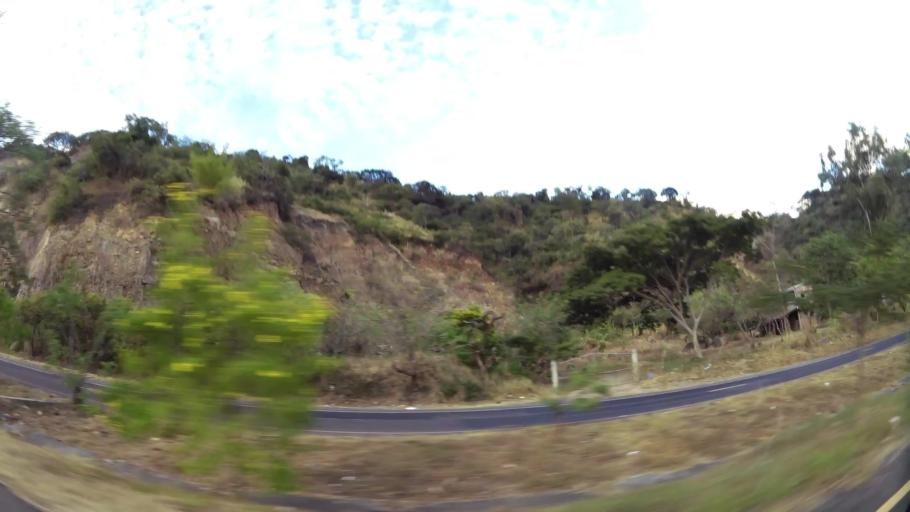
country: SV
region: San Vicente
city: Apastepeque
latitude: 13.6672
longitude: -88.8111
